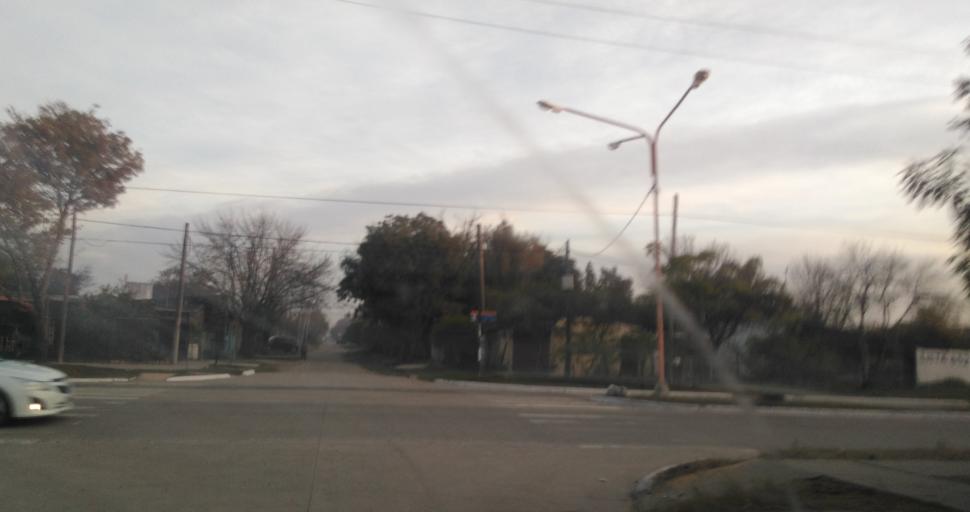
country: AR
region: Chaco
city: Resistencia
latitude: -27.4636
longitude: -59.0087
